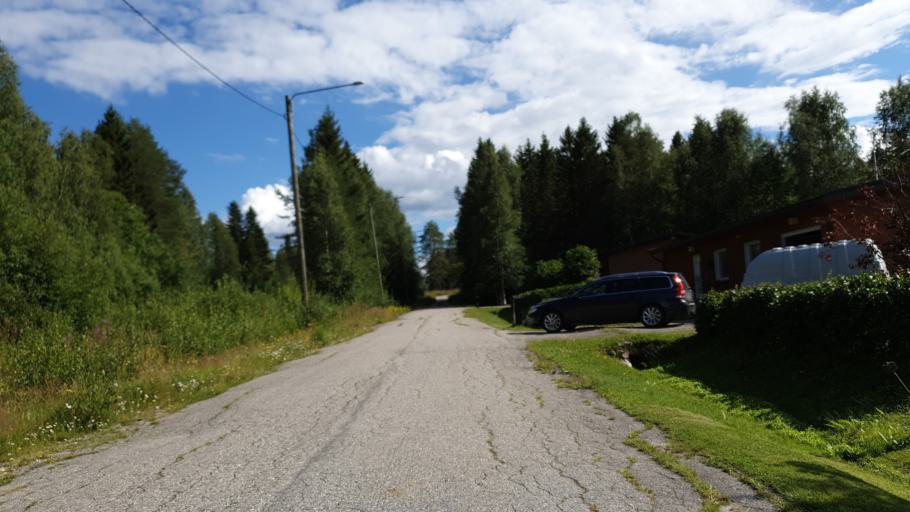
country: FI
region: Kainuu
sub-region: Kehys-Kainuu
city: Kuhmo
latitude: 64.1204
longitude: 29.4972
